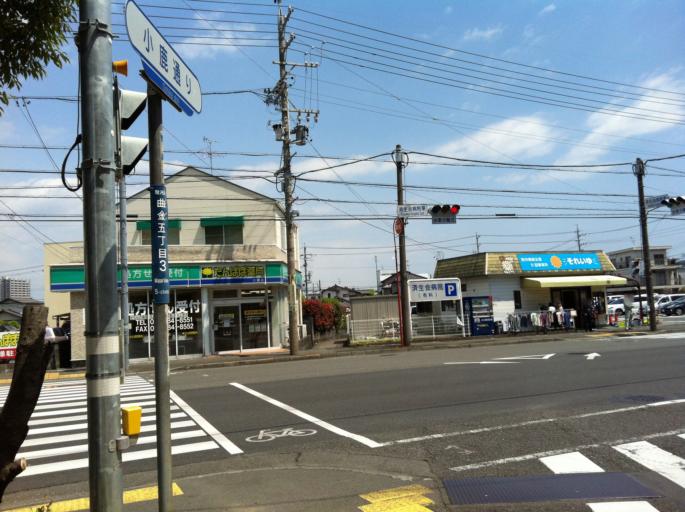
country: JP
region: Shizuoka
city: Shizuoka-shi
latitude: 34.9765
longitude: 138.4130
